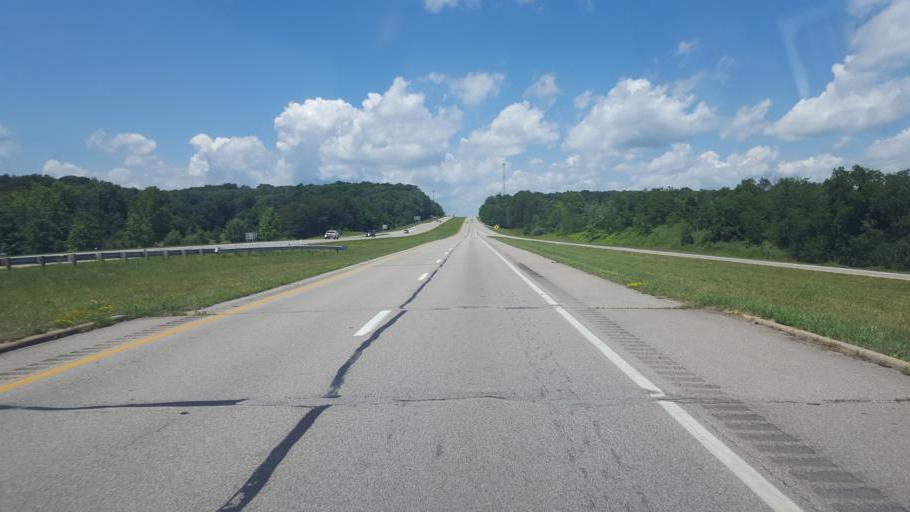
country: US
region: Ohio
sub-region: Gallia County
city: Gallipolis
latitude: 38.8771
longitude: -82.2983
